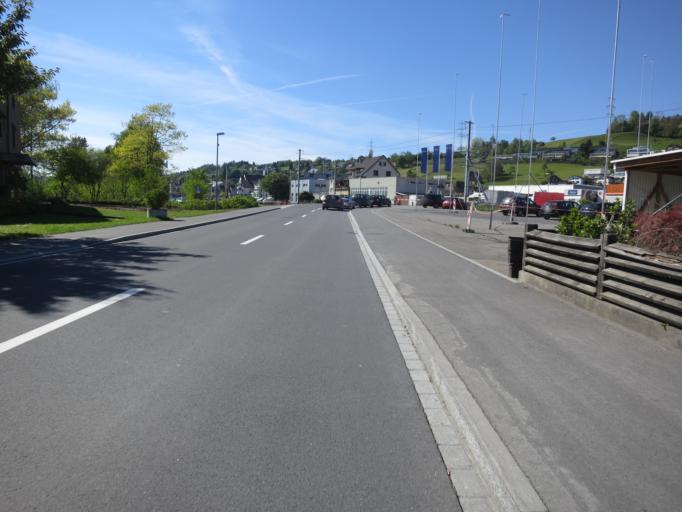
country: CH
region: Saint Gallen
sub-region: Wahlkreis See-Gaster
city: Schmerikon
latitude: 47.2245
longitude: 8.9493
